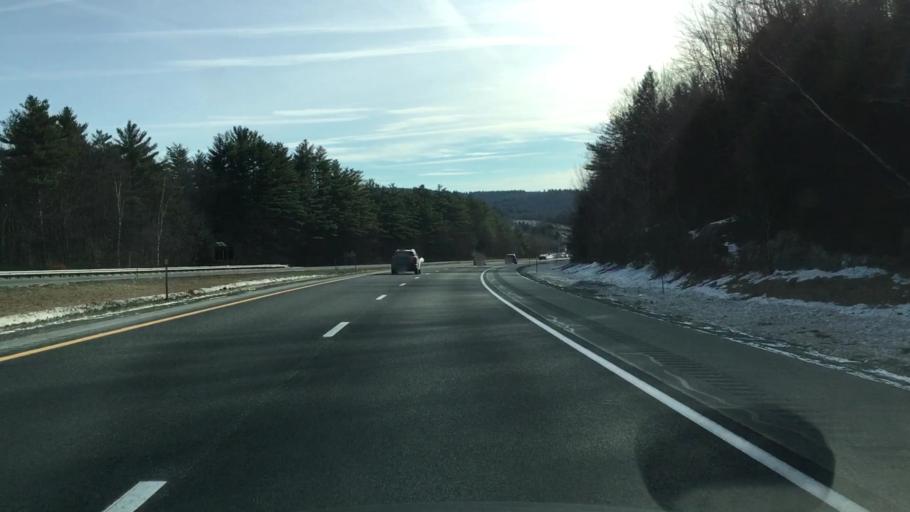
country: US
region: New Hampshire
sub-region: Sullivan County
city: Grantham
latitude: 43.5118
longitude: -72.1349
